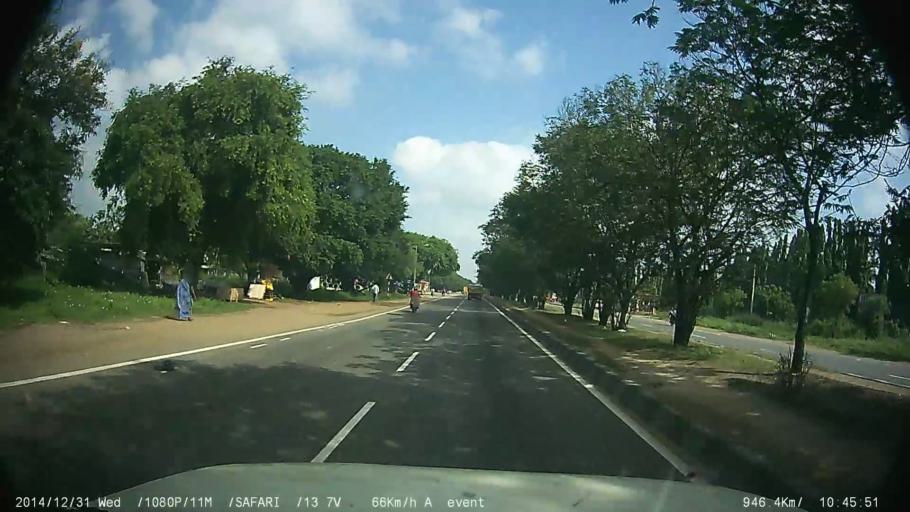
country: IN
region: Tamil Nadu
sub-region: Kancheepuram
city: Singapperumalkovil
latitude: 12.7885
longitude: 80.0160
